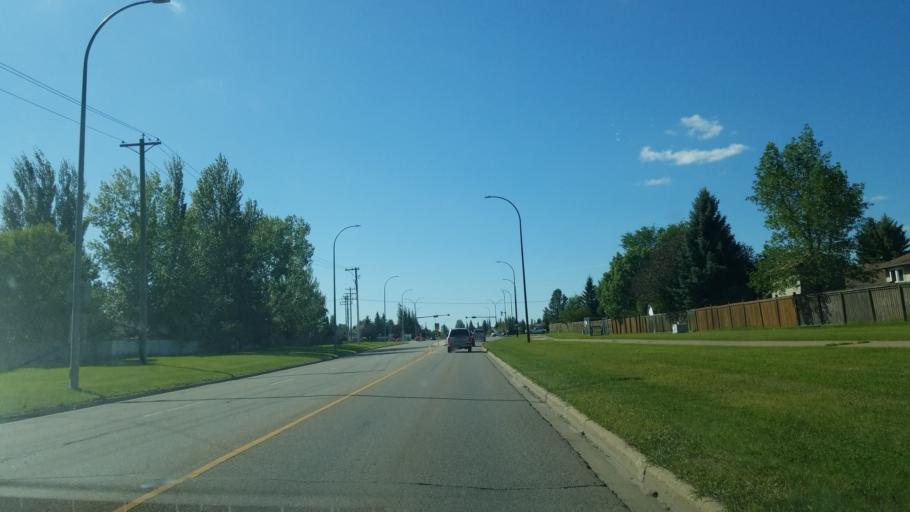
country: CA
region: Saskatchewan
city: Lloydminster
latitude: 53.2707
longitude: -110.0266
